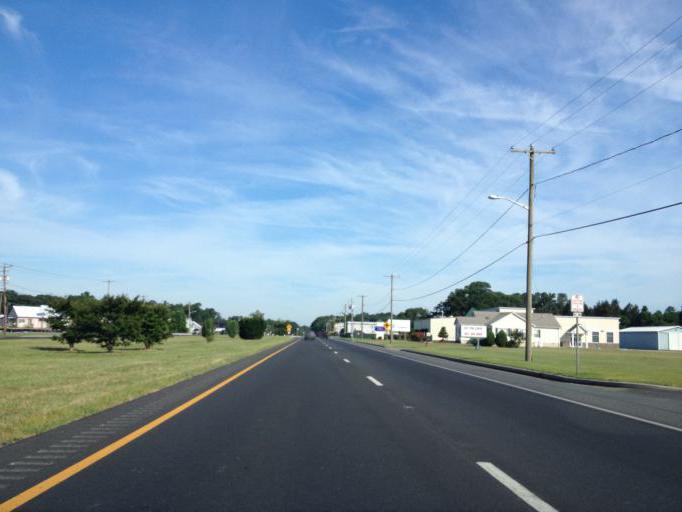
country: US
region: Delaware
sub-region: Sussex County
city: Millsboro
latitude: 38.5887
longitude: -75.3002
